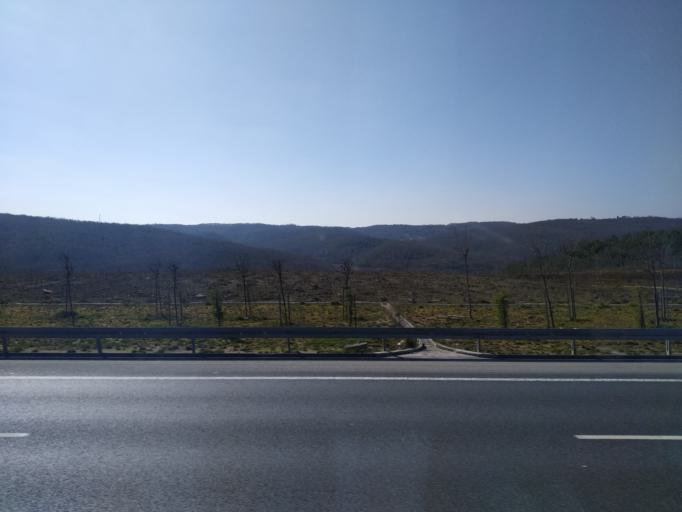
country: TR
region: Istanbul
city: Mahmut Sevket Pasa
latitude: 41.1777
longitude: 29.2386
